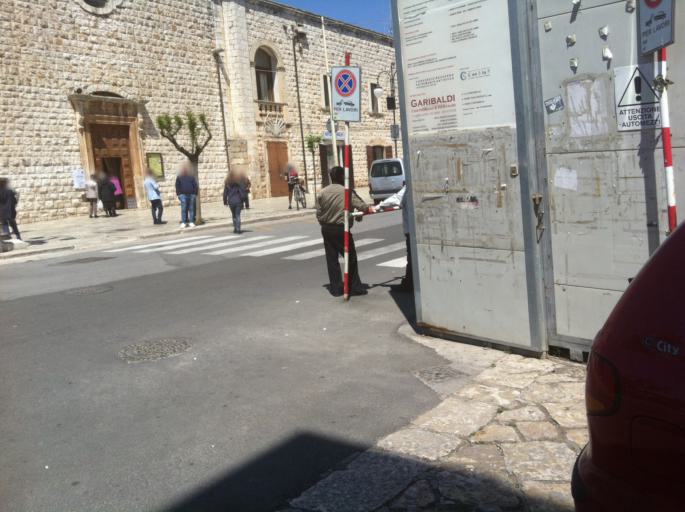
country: IT
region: Apulia
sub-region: Provincia di Bari
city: Putignano
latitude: 40.8496
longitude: 17.1213
